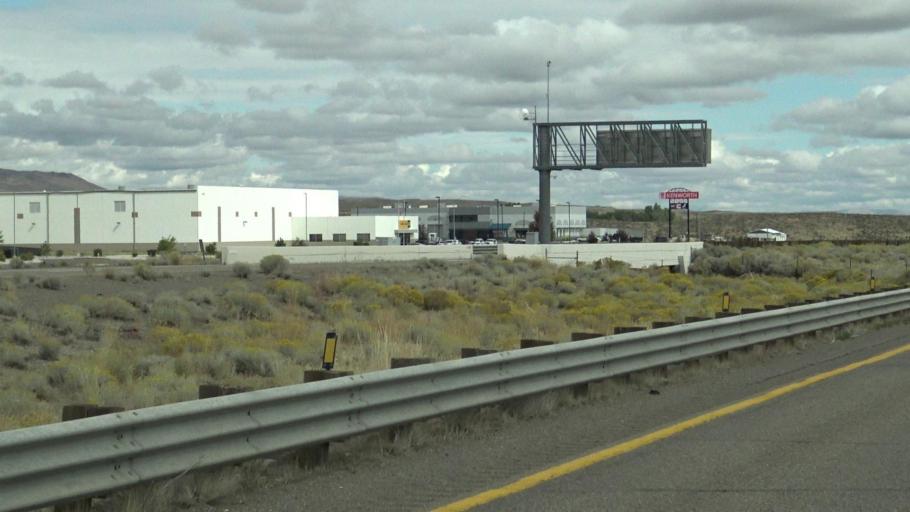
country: US
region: Nevada
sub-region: Elko County
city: Elko
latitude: 40.8643
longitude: -115.7341
